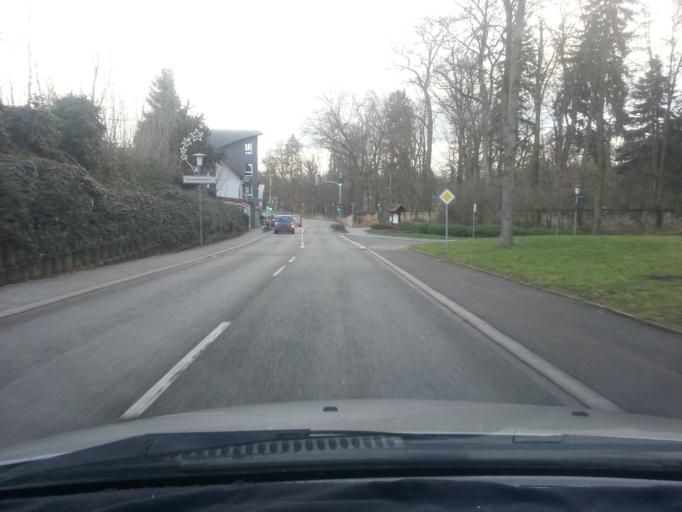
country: DE
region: Baden-Wuerttemberg
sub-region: Karlsruhe Region
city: Balzfeld
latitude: 49.2307
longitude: 8.7762
